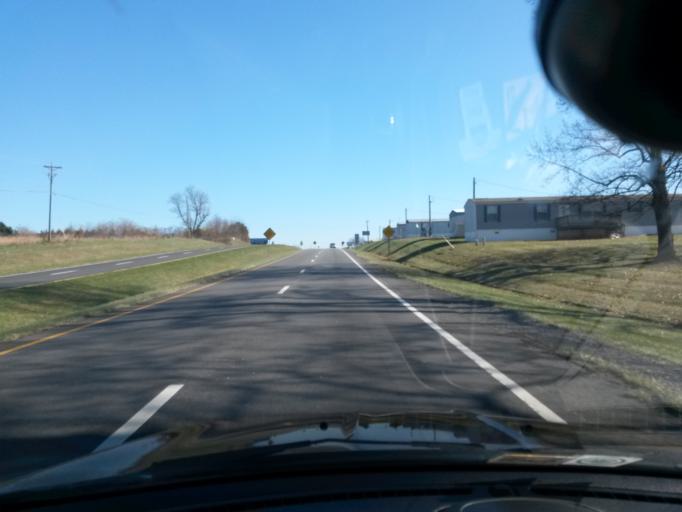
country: US
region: Virginia
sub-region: Bedford County
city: Forest
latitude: 37.3006
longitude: -79.3575
